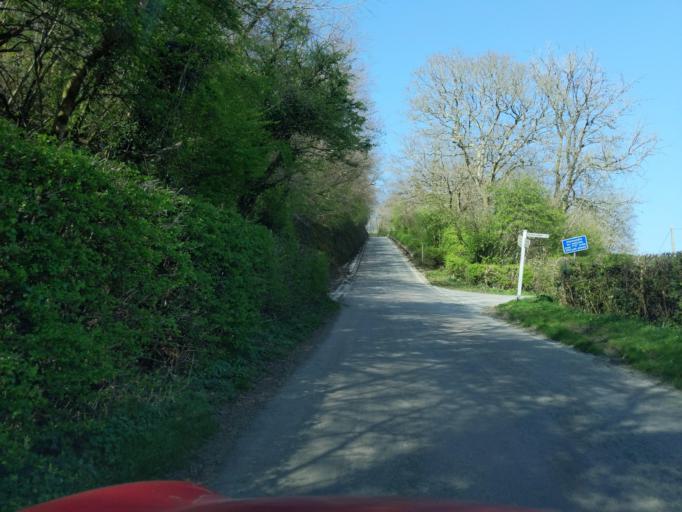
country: GB
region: England
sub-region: Devon
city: Horrabridge
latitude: 50.4681
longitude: -4.1339
